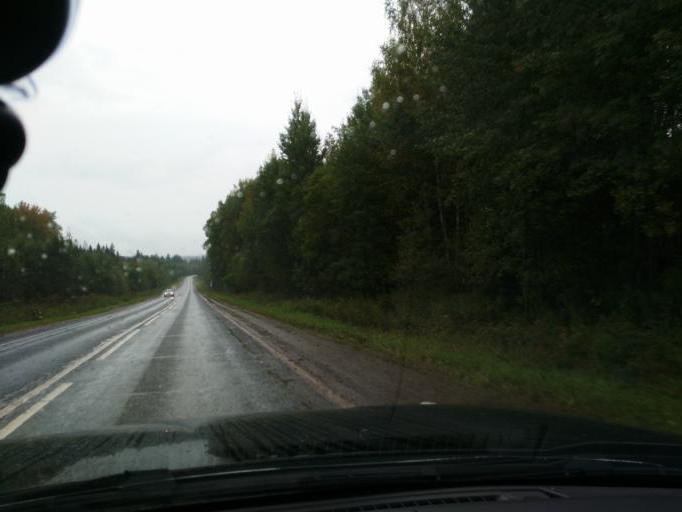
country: RU
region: Perm
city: Yugo-Kamskiy
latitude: 57.5204
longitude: 55.6852
